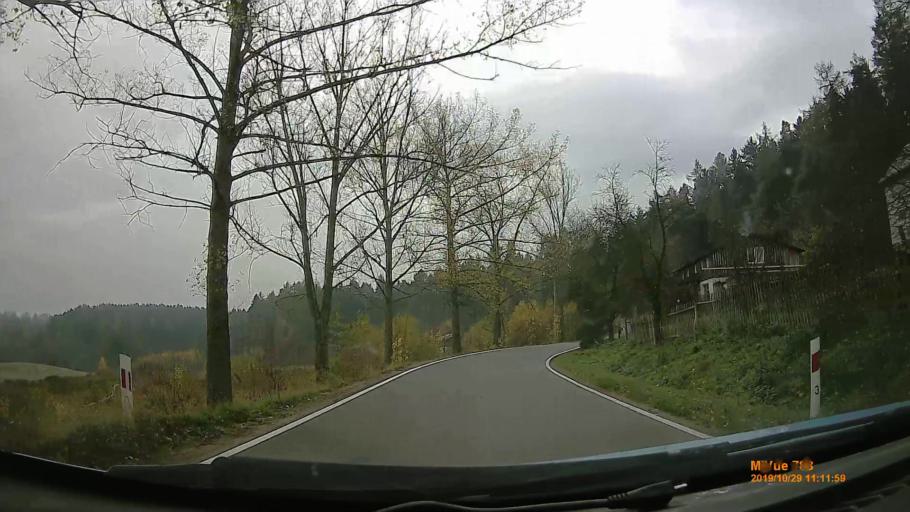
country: PL
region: Lower Silesian Voivodeship
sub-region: Powiat klodzki
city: Polanica-Zdroj
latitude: 50.4308
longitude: 16.5047
